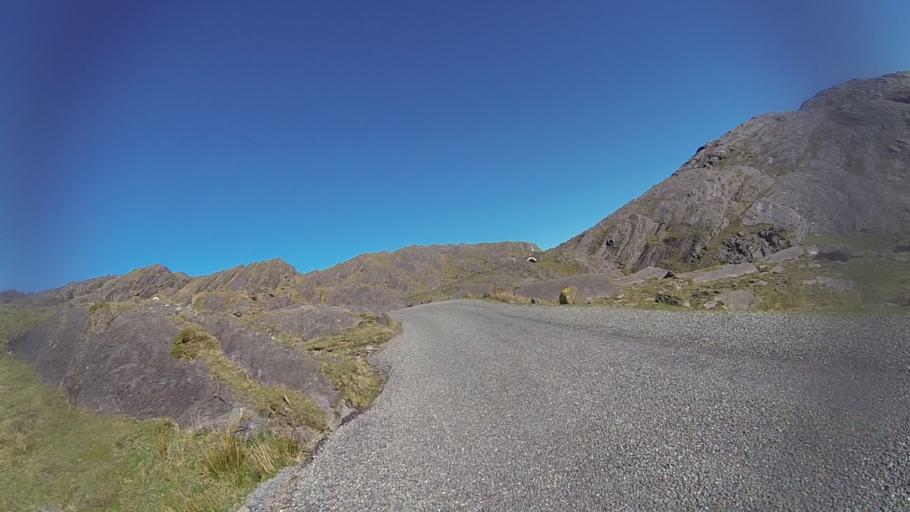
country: IE
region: Munster
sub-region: Ciarrai
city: Kenmare
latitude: 51.7185
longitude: -9.7550
